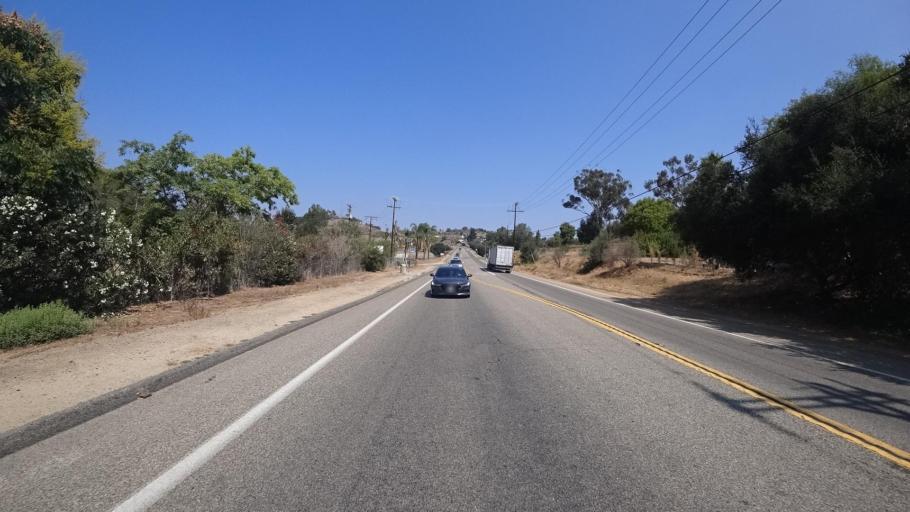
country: US
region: California
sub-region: San Diego County
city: Bonsall
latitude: 33.3129
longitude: -117.2301
